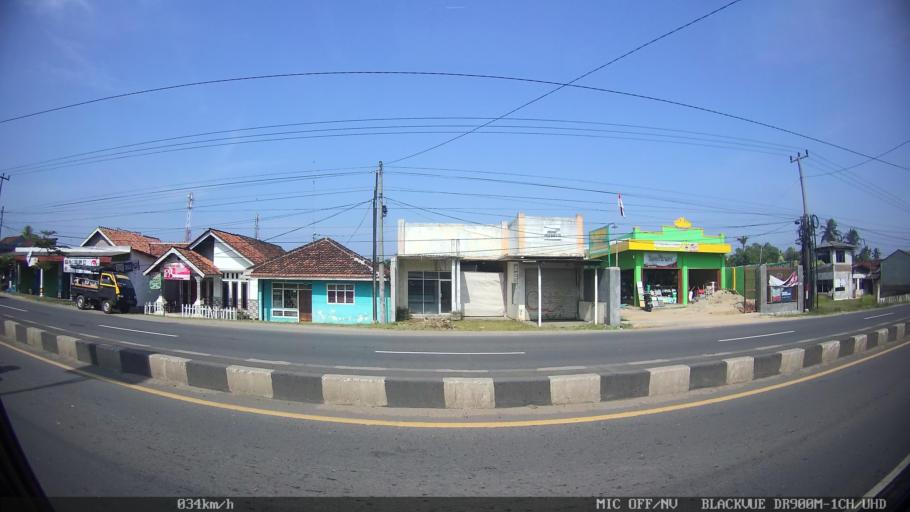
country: ID
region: Lampung
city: Natar
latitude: -5.2539
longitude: 105.1836
